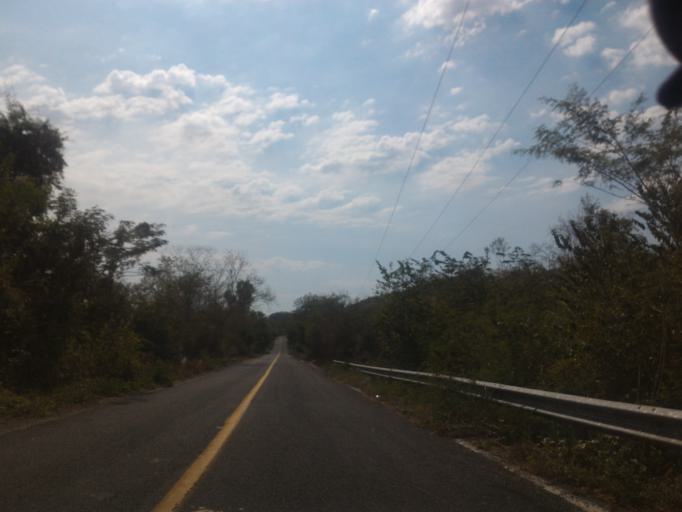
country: MX
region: Michoacan
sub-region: Coalcoman de Vazquez Pallares
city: Coalcoman de Vazquez Pallares
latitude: 18.2858
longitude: -103.3670
